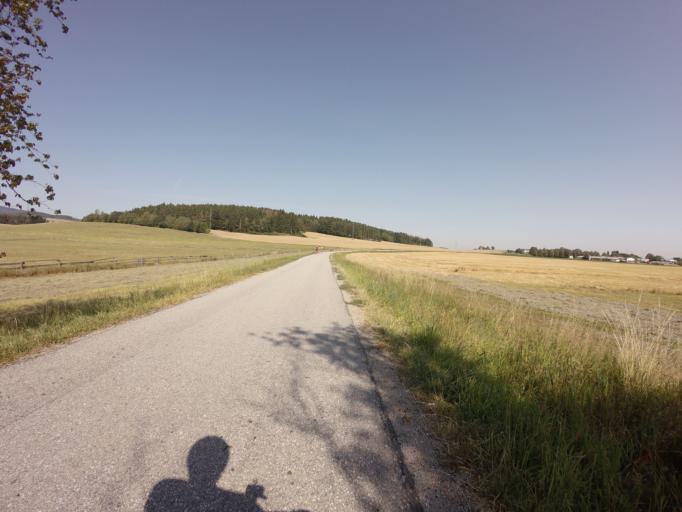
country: CZ
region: Jihocesky
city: Kamenny Ujezd
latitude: 48.8677
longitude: 14.3782
